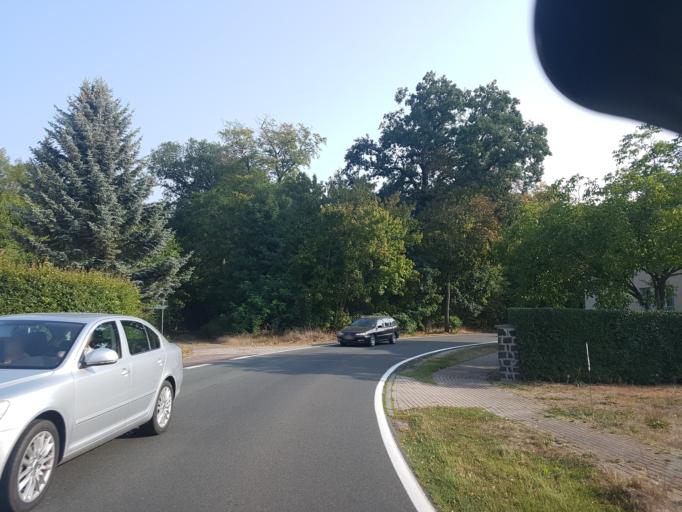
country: DE
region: Brandenburg
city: Wiesenburg
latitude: 52.0711
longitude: 12.3846
